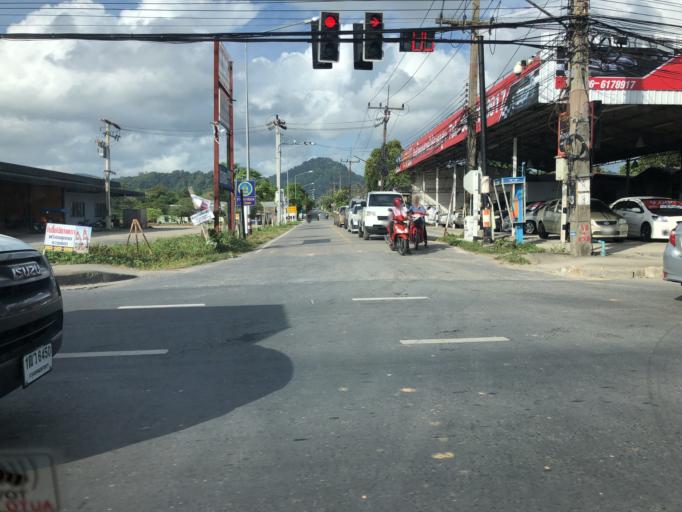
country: TH
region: Phuket
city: Thalang
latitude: 8.0073
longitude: 98.3425
